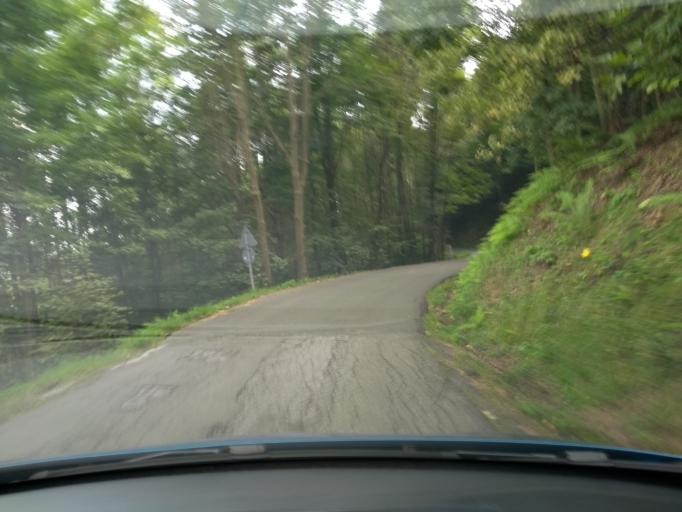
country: IT
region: Piedmont
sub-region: Provincia di Torino
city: Corio
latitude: 45.3320
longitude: 7.5149
